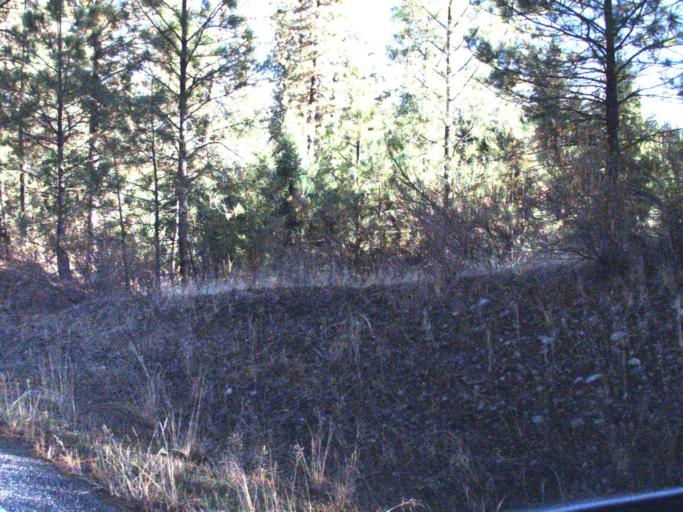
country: US
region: Washington
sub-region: Okanogan County
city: Coulee Dam
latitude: 48.0559
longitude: -118.6712
